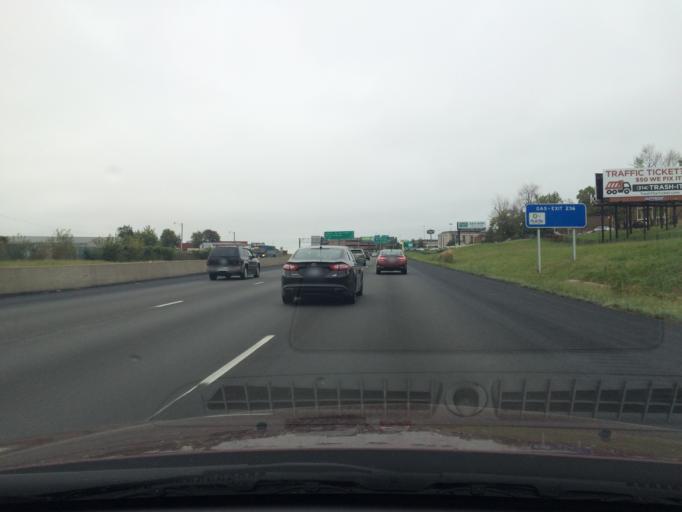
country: US
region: Missouri
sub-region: Saint Louis County
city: Saint Ann
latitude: 38.7420
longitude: -90.3768
